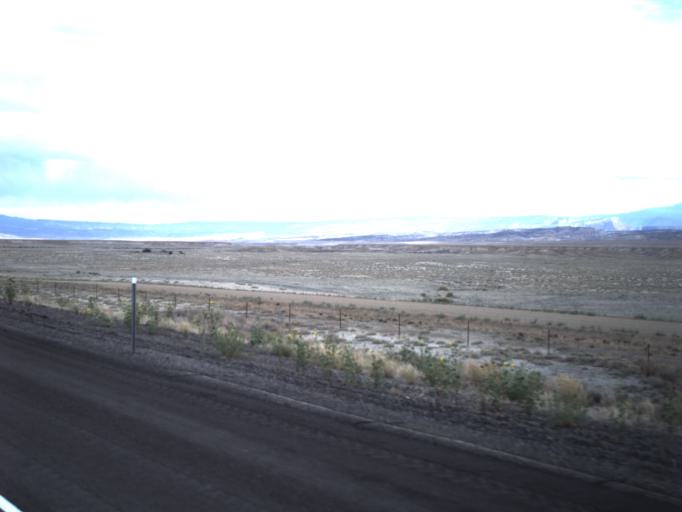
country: US
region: Utah
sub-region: Grand County
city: Moab
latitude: 38.9325
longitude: -109.4407
